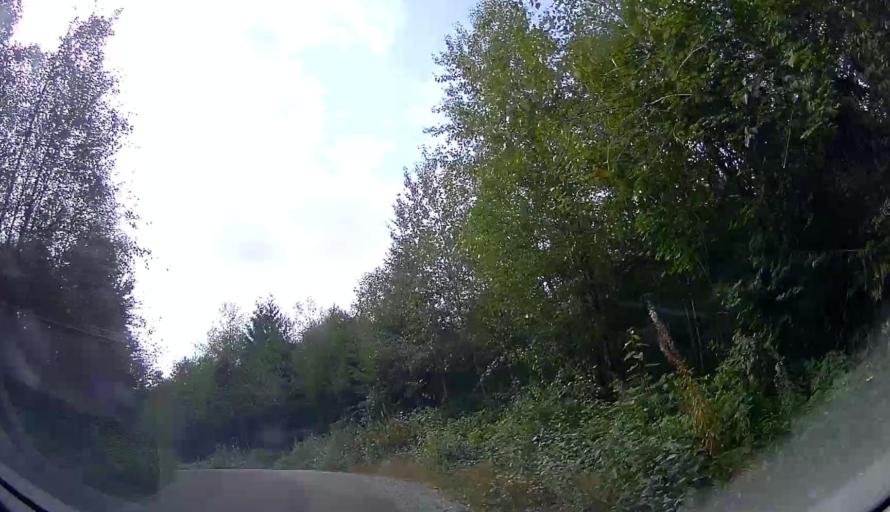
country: US
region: Washington
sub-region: Whatcom County
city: Sudden Valley
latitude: 48.6199
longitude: -122.3706
